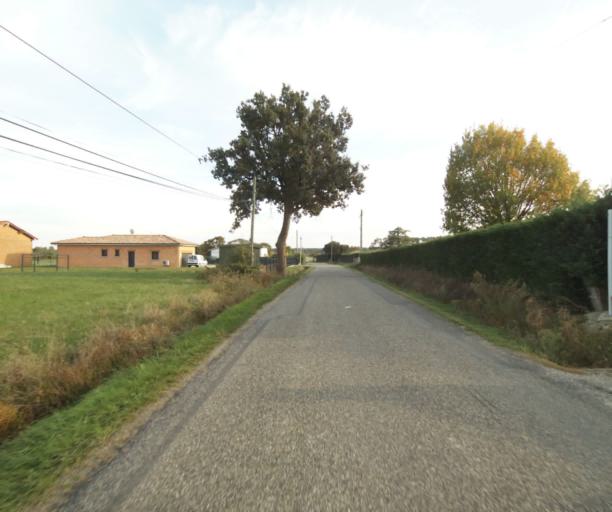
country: FR
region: Midi-Pyrenees
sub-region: Departement du Tarn-et-Garonne
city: Campsas
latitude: 43.8837
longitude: 1.3359
